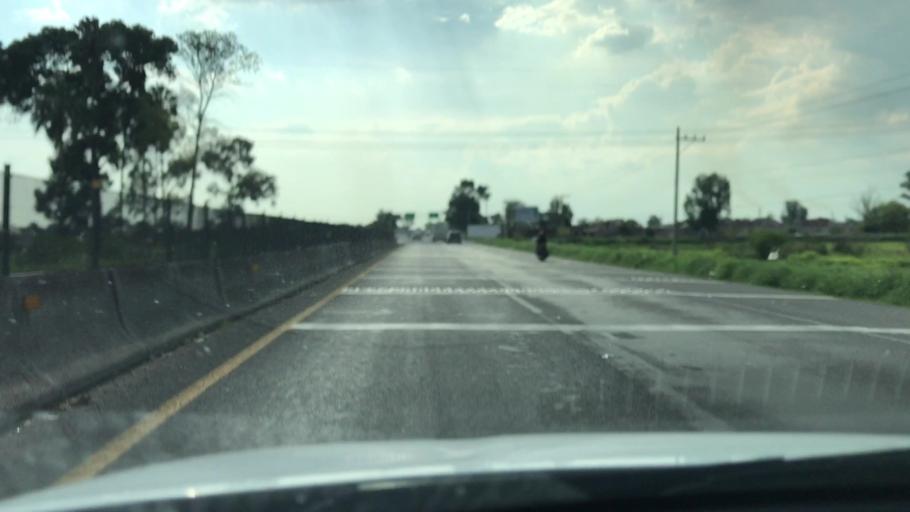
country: MX
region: Guanajuato
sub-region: Salamanca
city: El Divisador
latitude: 20.5573
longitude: -101.1623
